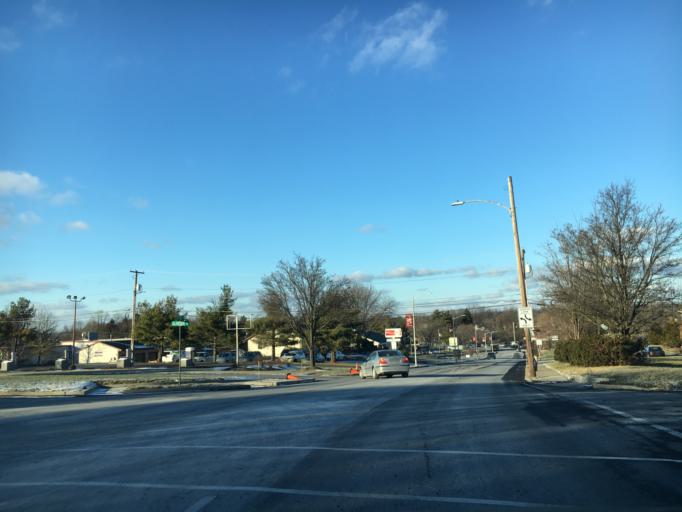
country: US
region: Pennsylvania
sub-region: Lehigh County
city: Hokendauqua
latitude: 40.6519
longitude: -75.4969
